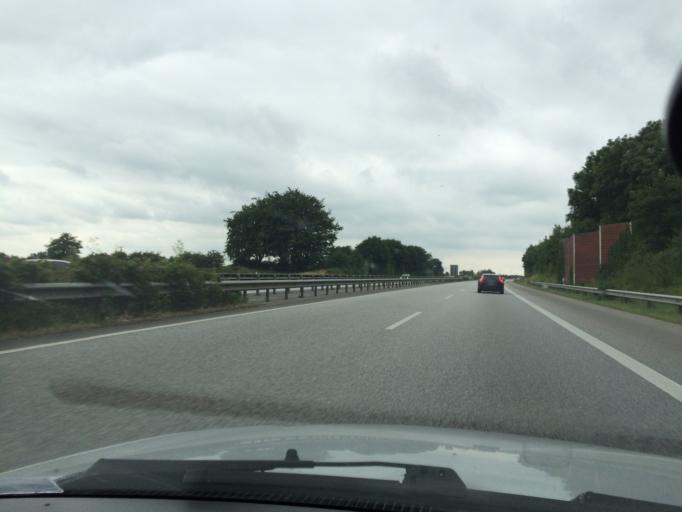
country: DE
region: Schleswig-Holstein
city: Jarplund-Weding
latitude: 54.7286
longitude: 9.3934
